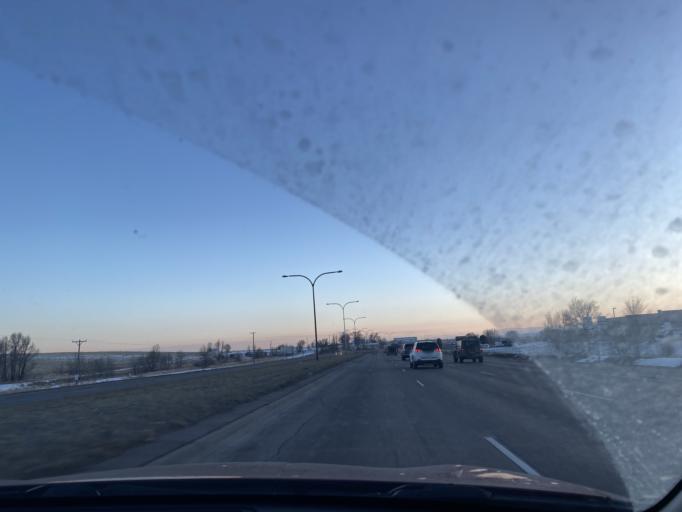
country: US
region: Colorado
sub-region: El Paso County
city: Cimarron Hills
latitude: 38.8348
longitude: -104.7209
